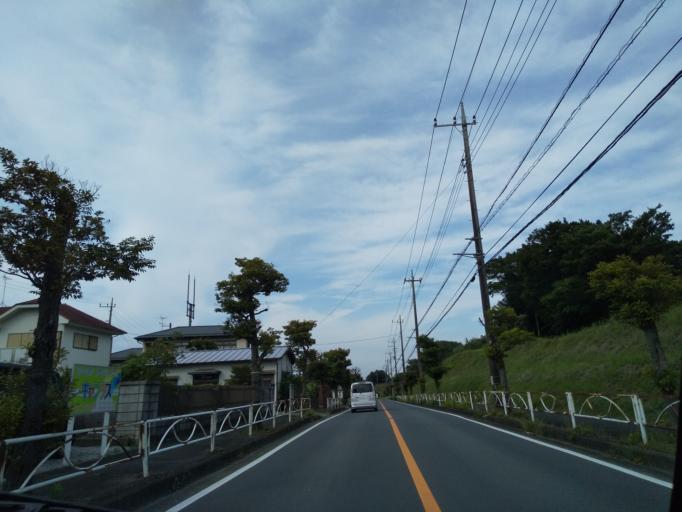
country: JP
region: Kanagawa
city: Atsugi
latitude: 35.4764
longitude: 139.3147
